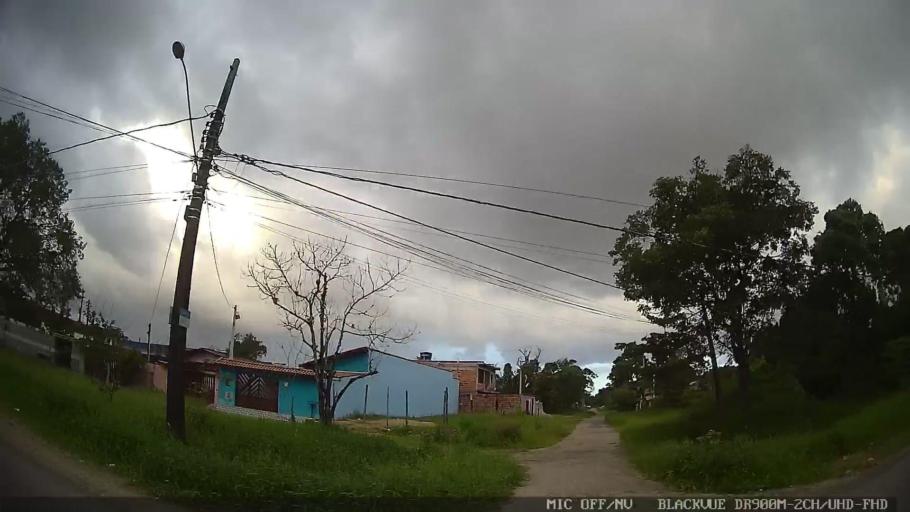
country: BR
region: Sao Paulo
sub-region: Itanhaem
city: Itanhaem
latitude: -24.1547
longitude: -46.7801
